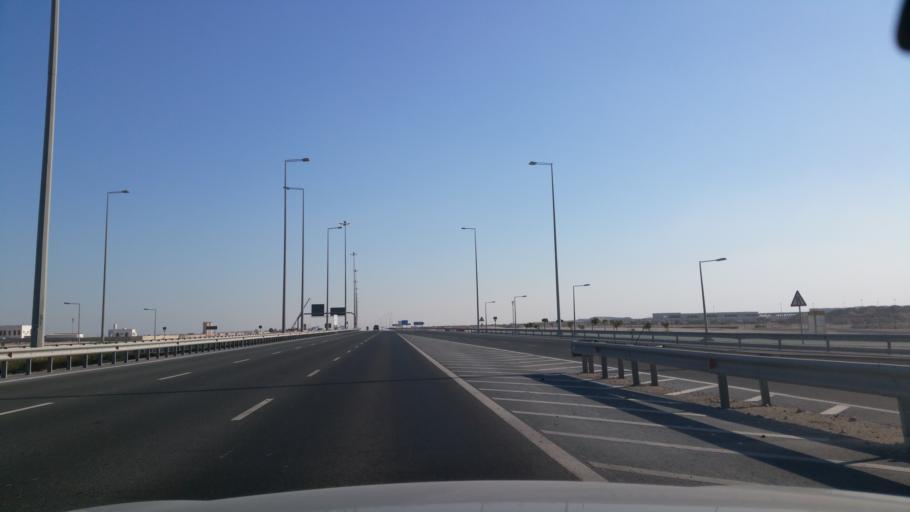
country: QA
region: Al Wakrah
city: Al Wukayr
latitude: 25.1593
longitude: 51.4728
